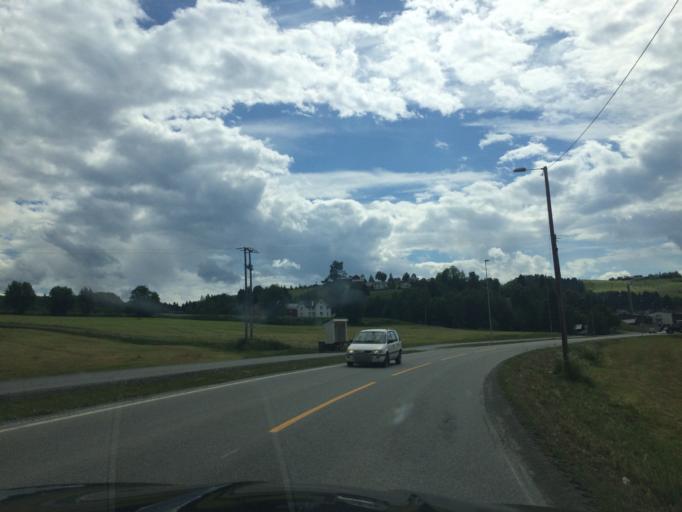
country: NO
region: Sor-Trondelag
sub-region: Selbu
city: Mebonden
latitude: 63.2454
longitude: 11.0909
